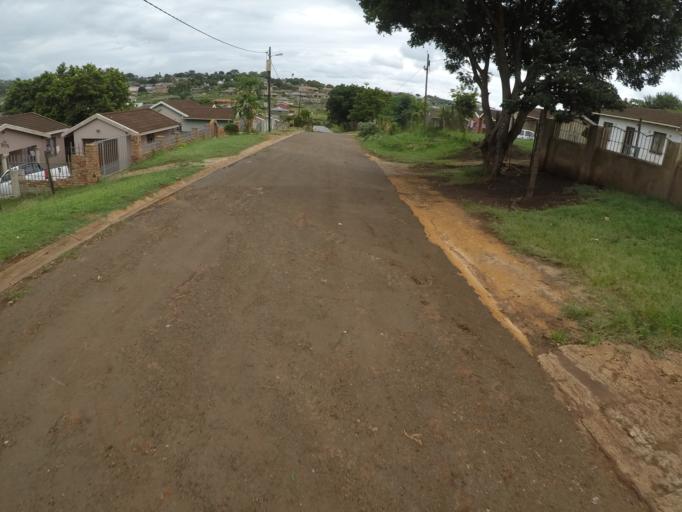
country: ZA
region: KwaZulu-Natal
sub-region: uThungulu District Municipality
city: Empangeni
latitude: -28.7804
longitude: 31.8570
